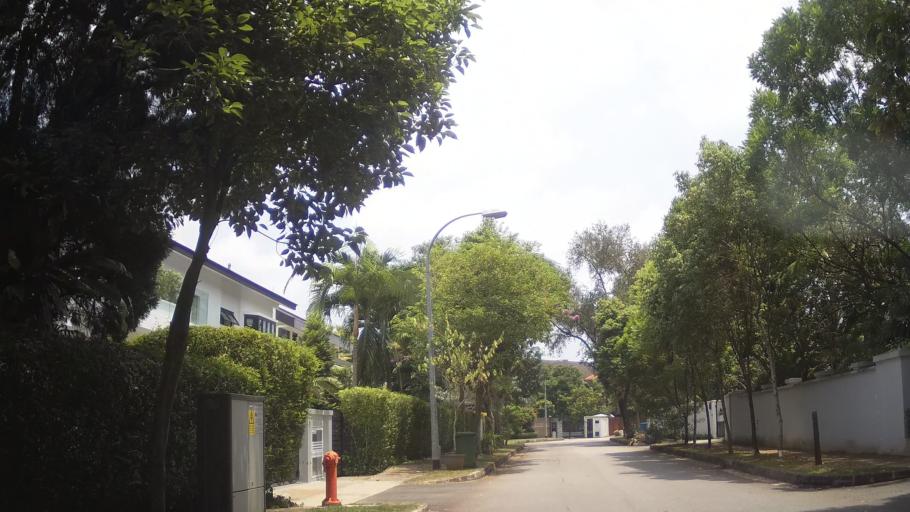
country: MY
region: Johor
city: Johor Bahru
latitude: 1.3723
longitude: 103.7702
